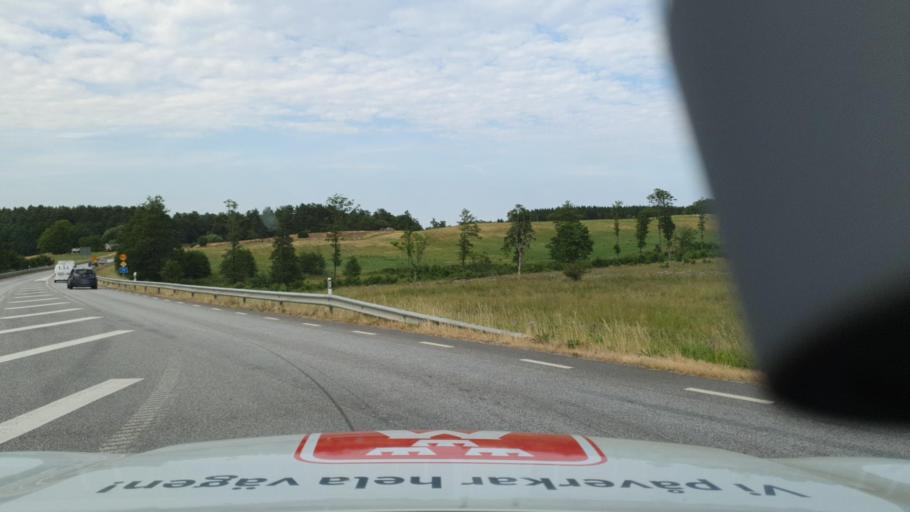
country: SE
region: Skane
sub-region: Kristianstads Kommun
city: Degeberga
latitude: 55.6975
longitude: 14.0399
